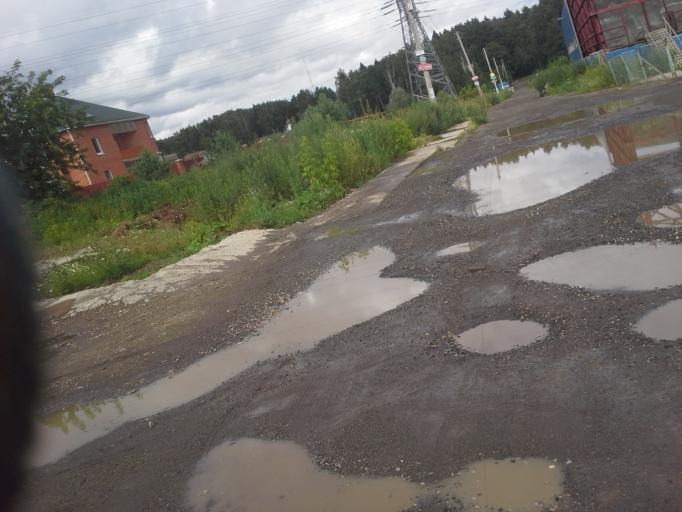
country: RU
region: Moskovskaya
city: Lesnoy Gorodok
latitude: 55.6367
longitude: 37.2321
